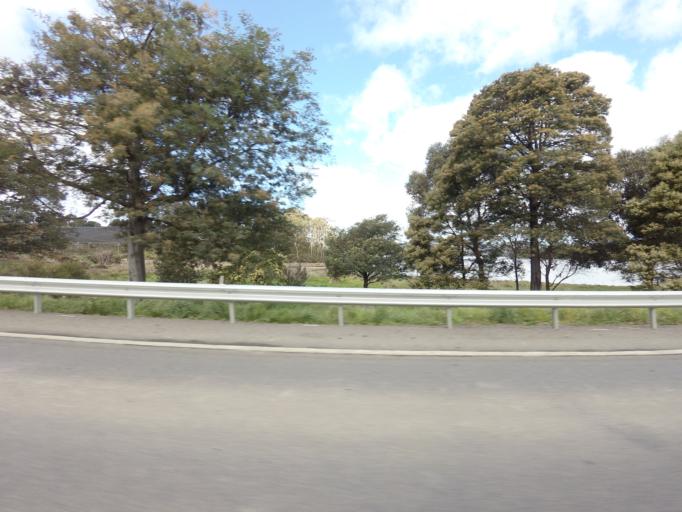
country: AU
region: Tasmania
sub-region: Huon Valley
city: Geeveston
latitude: -43.1375
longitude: 146.9726
